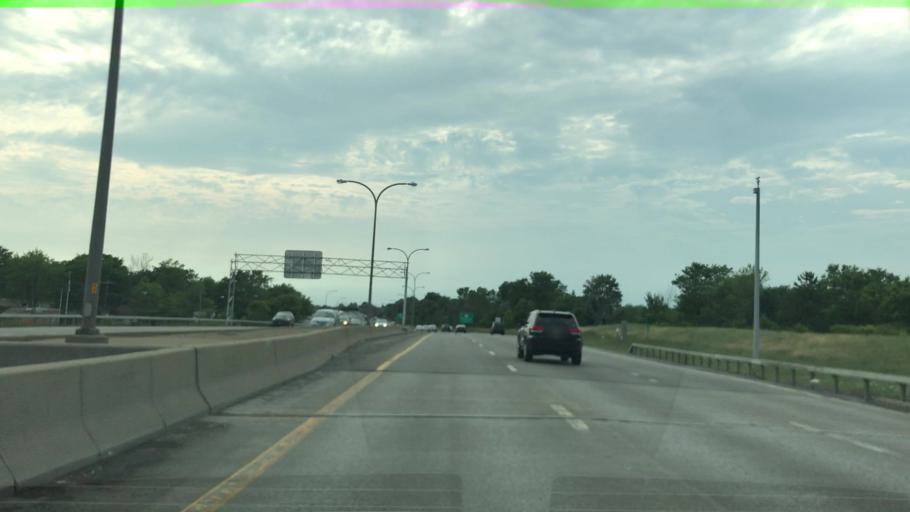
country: US
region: New York
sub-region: Erie County
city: Cheektowaga
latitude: 42.9328
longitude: -78.7719
